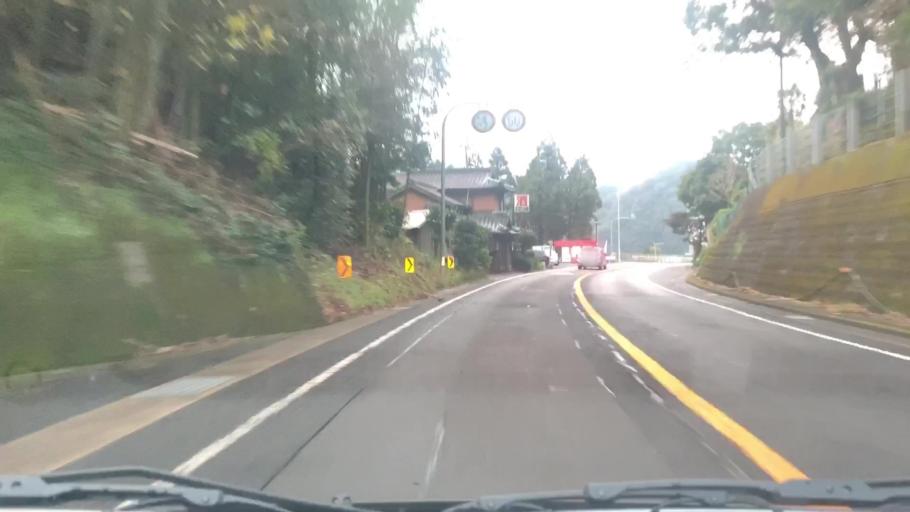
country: JP
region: Saga Prefecture
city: Ureshinomachi-shimojuku
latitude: 33.0625
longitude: 129.9601
